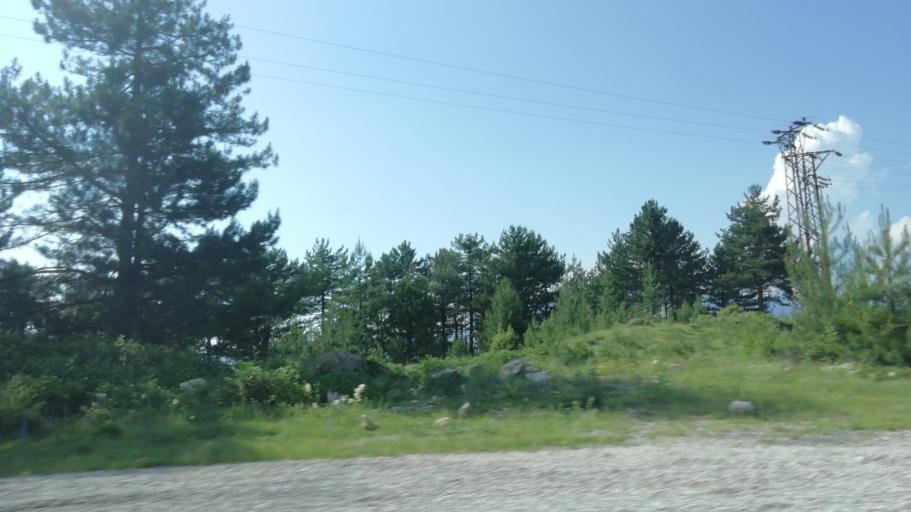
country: TR
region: Karabuk
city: Karabuk
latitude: 41.1204
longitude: 32.5818
